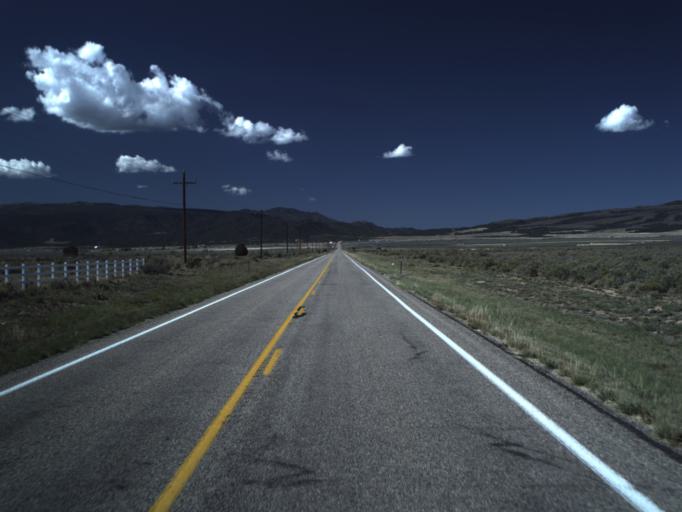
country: US
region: Utah
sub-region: Iron County
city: Cedar City
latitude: 37.6735
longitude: -113.1857
